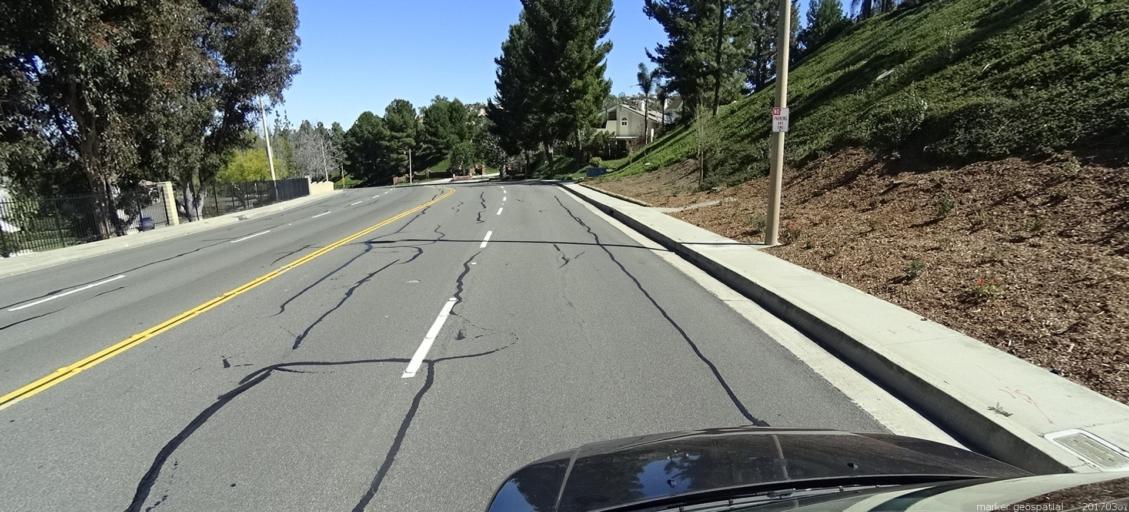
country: US
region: California
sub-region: Orange County
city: Villa Park
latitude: 33.8371
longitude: -117.8175
